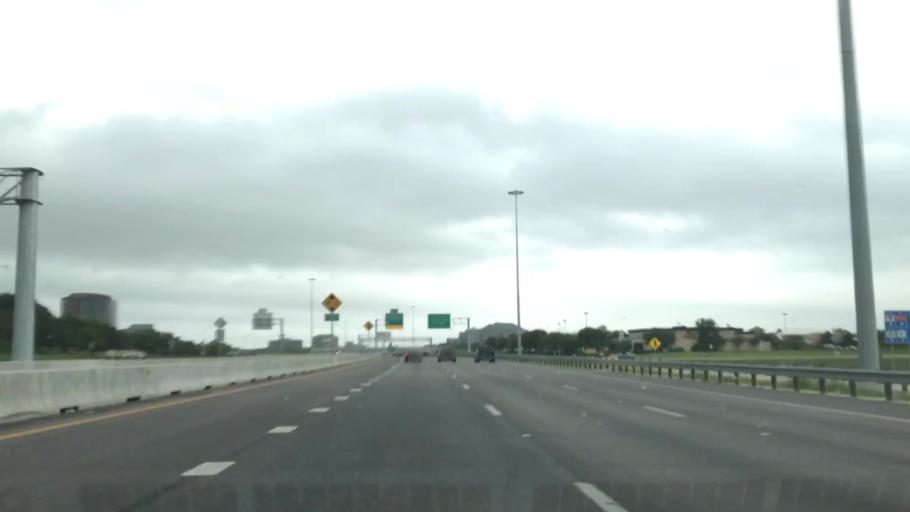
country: US
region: Texas
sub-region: Dallas County
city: Farmers Branch
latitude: 32.8870
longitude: -96.9561
